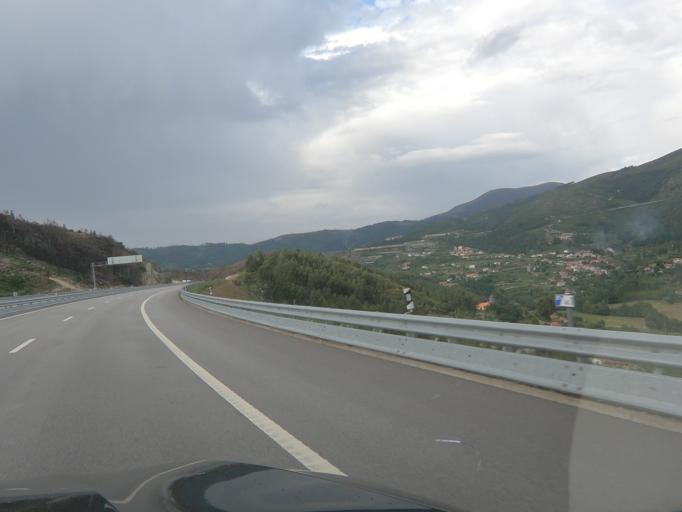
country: PT
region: Porto
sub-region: Amarante
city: Amarante
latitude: 41.2523
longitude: -7.9969
